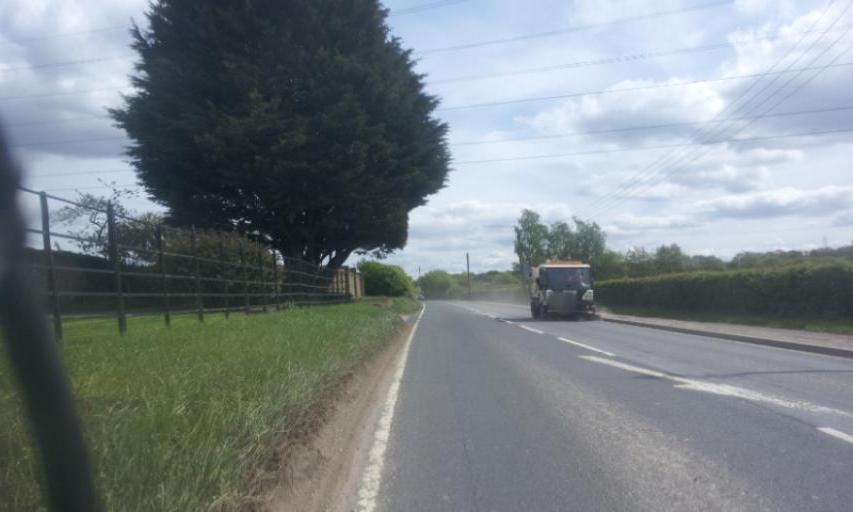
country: GB
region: England
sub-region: Kent
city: Longfield
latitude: 51.4044
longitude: 0.2842
